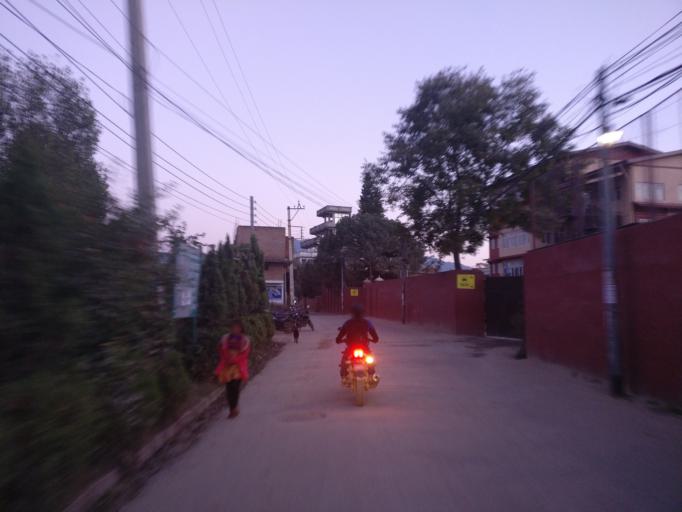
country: NP
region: Central Region
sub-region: Bagmati Zone
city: Patan
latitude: 27.6501
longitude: 85.3221
